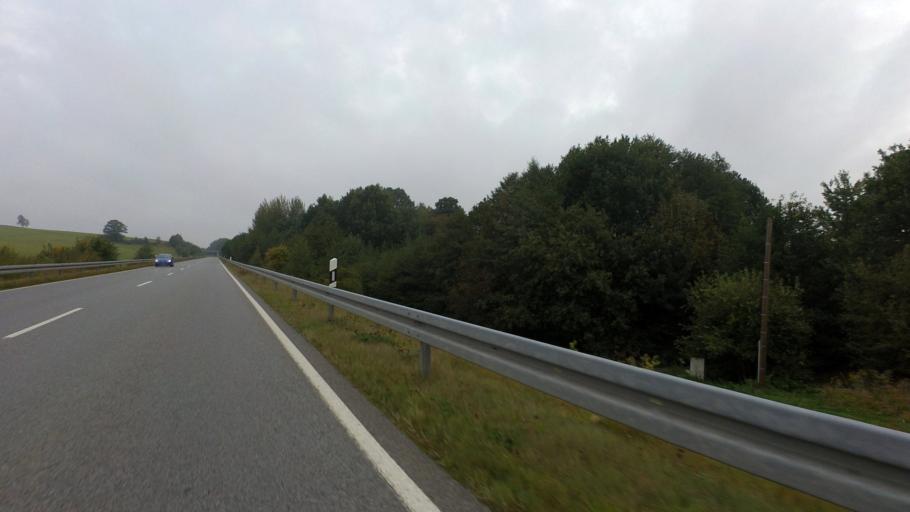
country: DE
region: Saxony
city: Berthelsdorf
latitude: 51.0475
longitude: 14.2116
